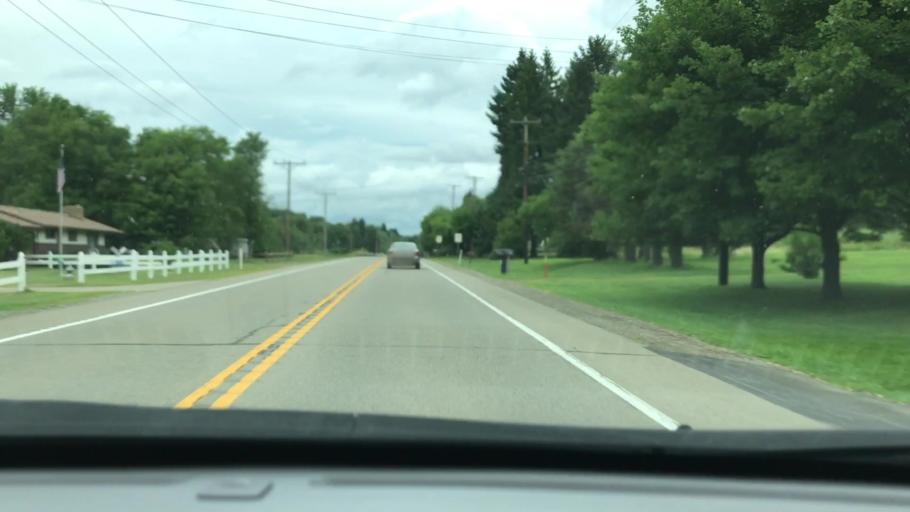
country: US
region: Pennsylvania
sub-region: Elk County
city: Johnsonburg
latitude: 41.5043
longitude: -78.6794
